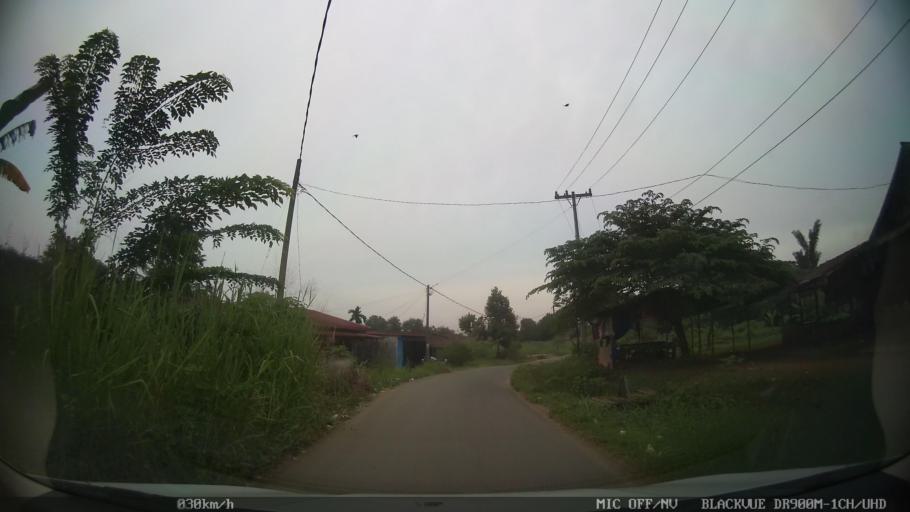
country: ID
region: North Sumatra
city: Deli Tua
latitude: 3.5435
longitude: 98.7283
